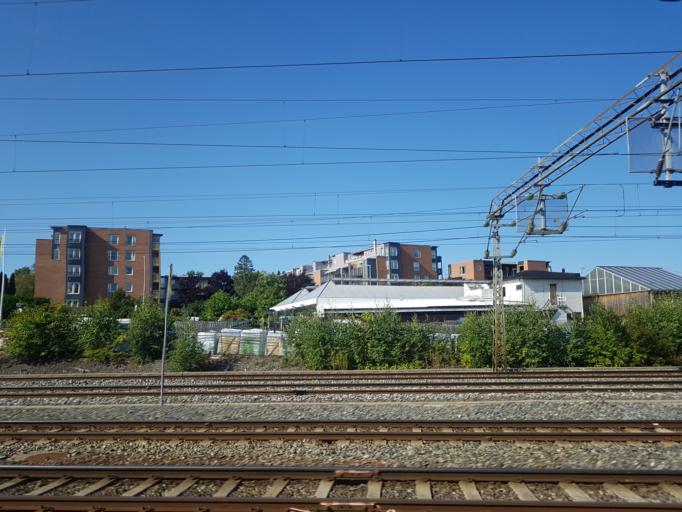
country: NO
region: Oslo
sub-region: Oslo
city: Sjolyststranda
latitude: 59.9229
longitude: 10.6703
